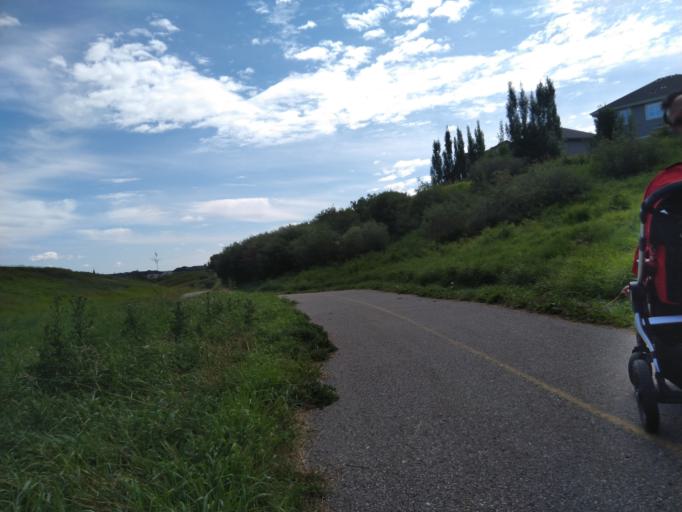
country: CA
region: Alberta
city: Calgary
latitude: 51.1625
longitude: -114.1383
